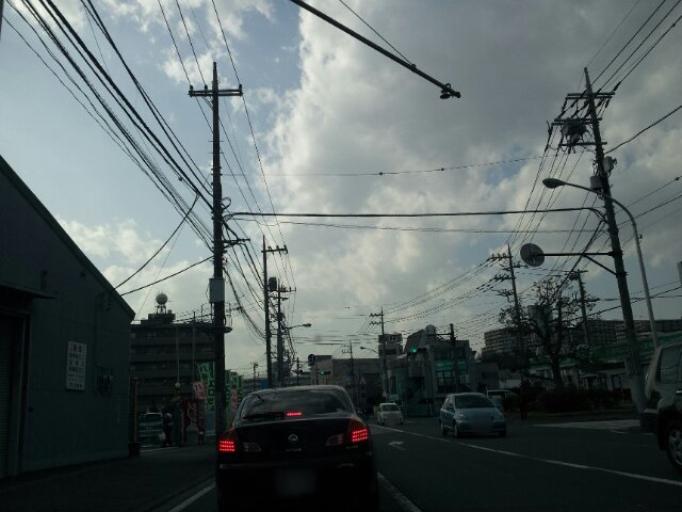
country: JP
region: Kanagawa
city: Yokohama
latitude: 35.4209
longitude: 139.5582
